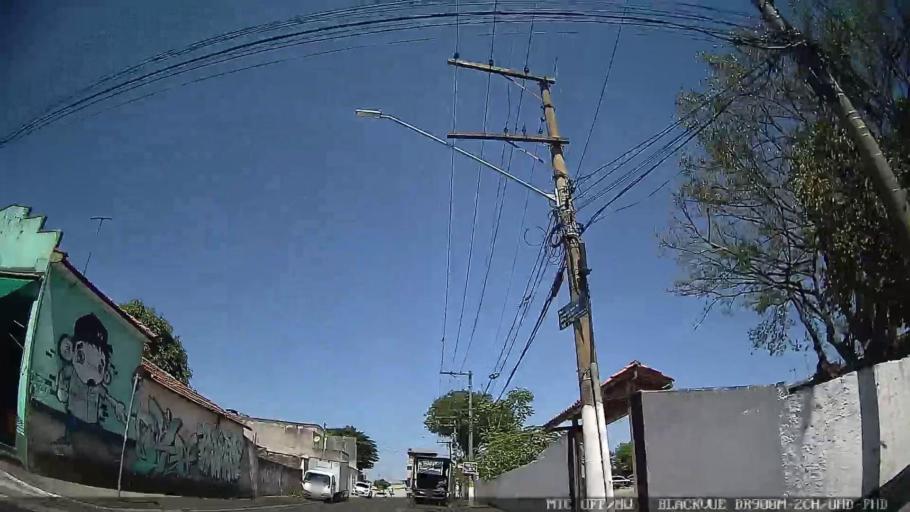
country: BR
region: Sao Paulo
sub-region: Sao Caetano Do Sul
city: Sao Caetano do Sul
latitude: -23.5791
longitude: -46.5177
